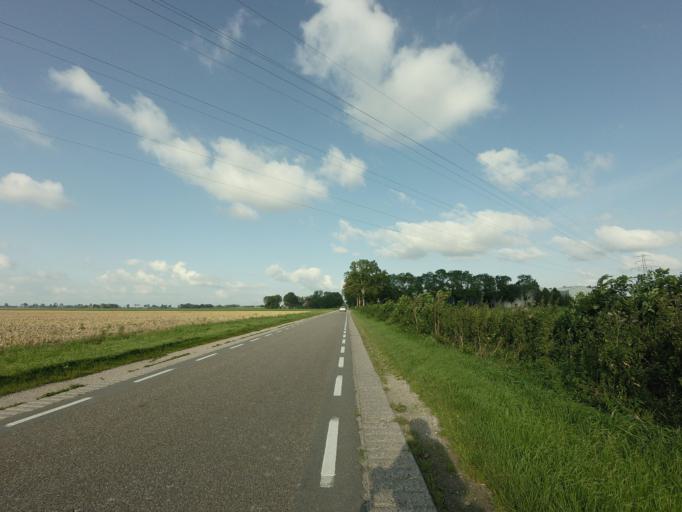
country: NL
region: Flevoland
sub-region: Gemeente Noordoostpolder
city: Ens
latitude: 52.6736
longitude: 5.8067
